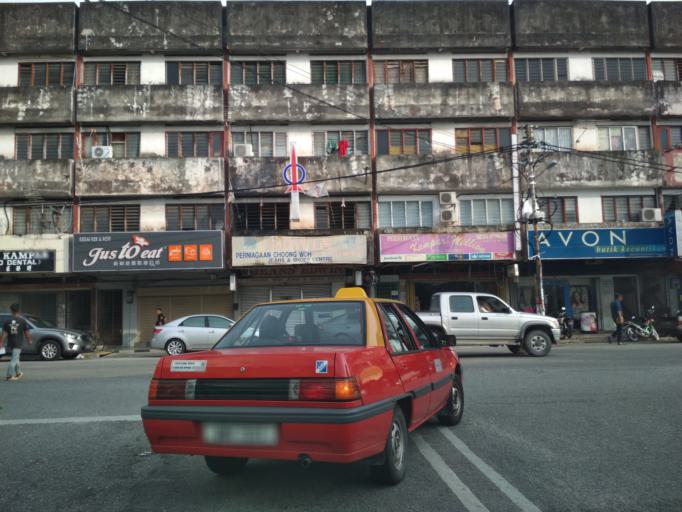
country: MY
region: Perak
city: Kampar
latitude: 4.3116
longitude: 101.1517
